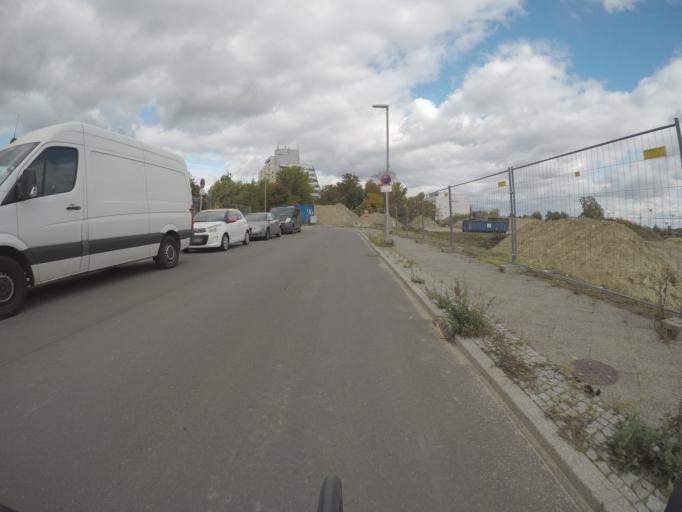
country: DE
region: Berlin
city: Hakenfelde
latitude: 52.5511
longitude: 13.2131
